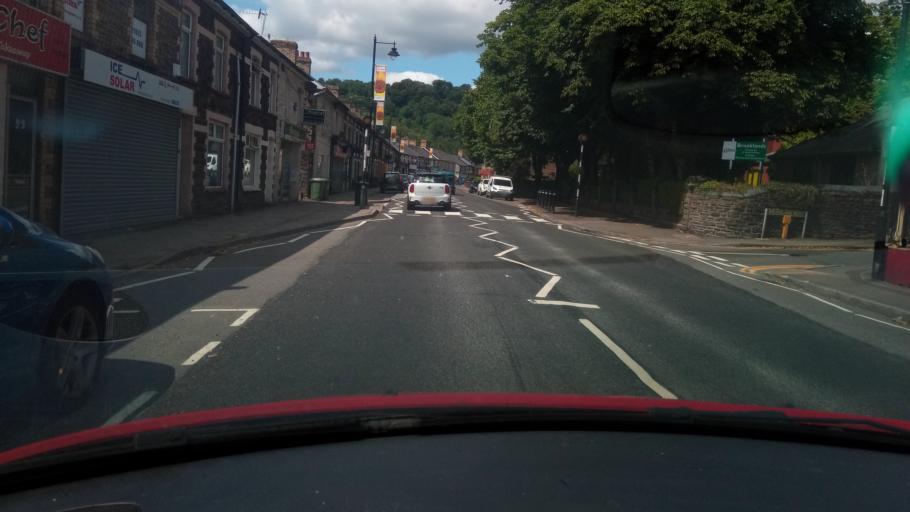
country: GB
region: Wales
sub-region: Caerphilly County Borough
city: Risca
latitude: 51.6042
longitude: -3.0959
